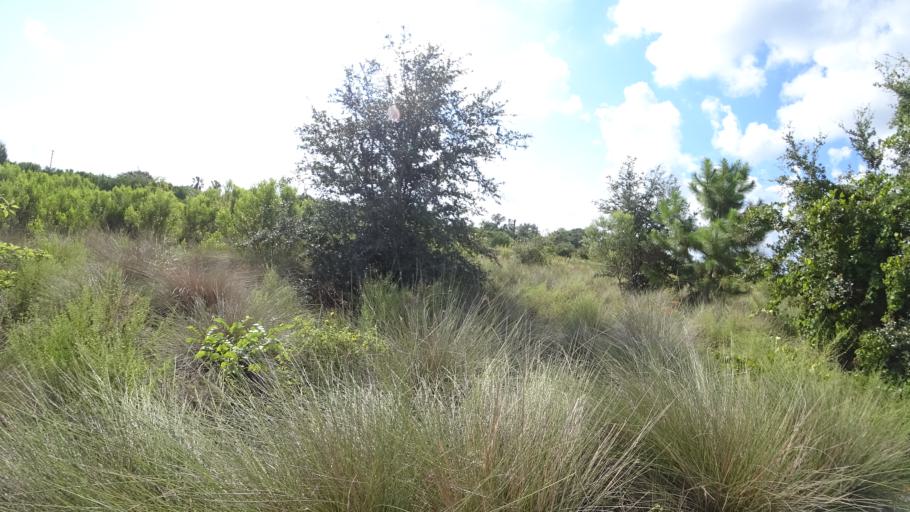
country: US
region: Florida
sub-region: Manatee County
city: Cortez
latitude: 27.4984
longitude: -82.6782
